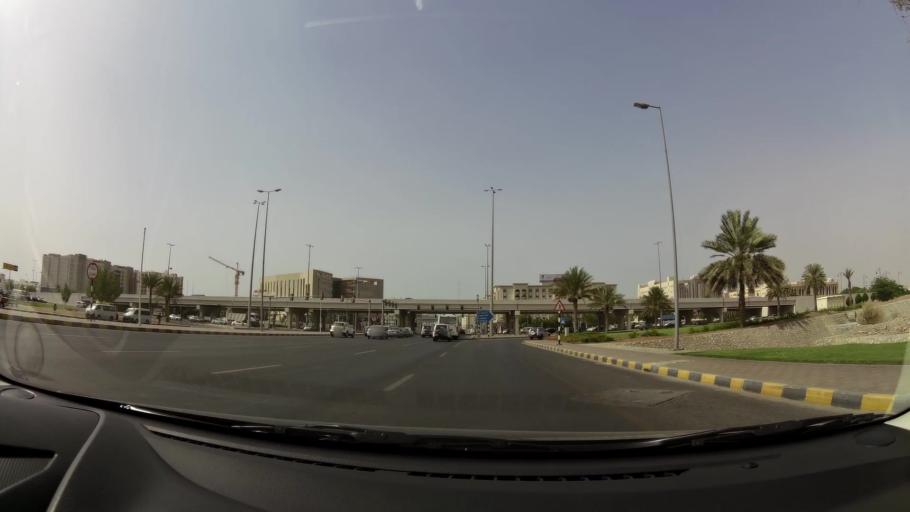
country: OM
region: Muhafazat Masqat
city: Bawshar
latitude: 23.5869
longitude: 58.3826
